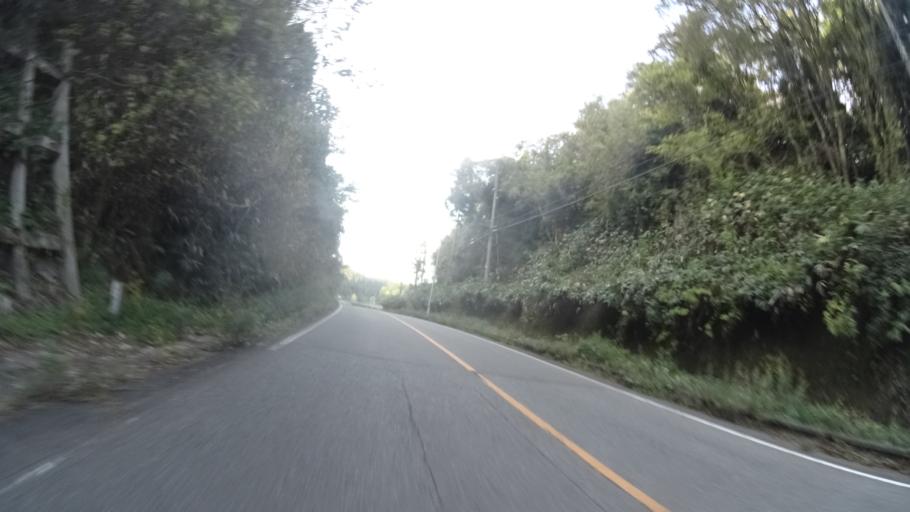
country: JP
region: Ishikawa
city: Nanao
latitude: 37.1830
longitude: 136.7145
